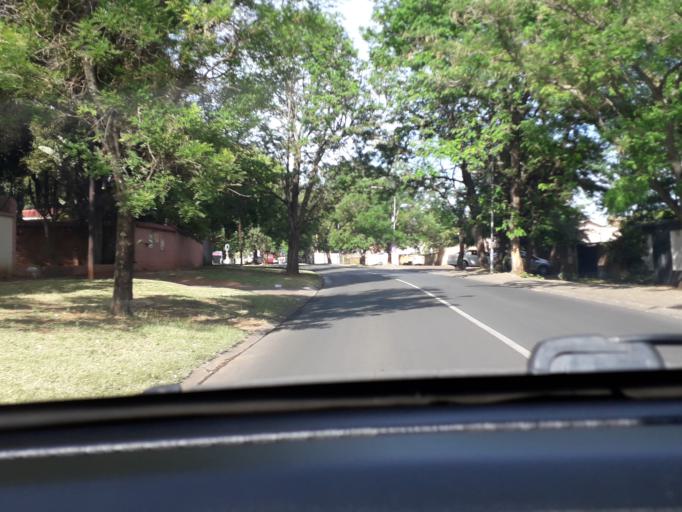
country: ZA
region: Gauteng
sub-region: City of Johannesburg Metropolitan Municipality
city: Modderfontein
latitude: -26.1359
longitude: 28.1055
